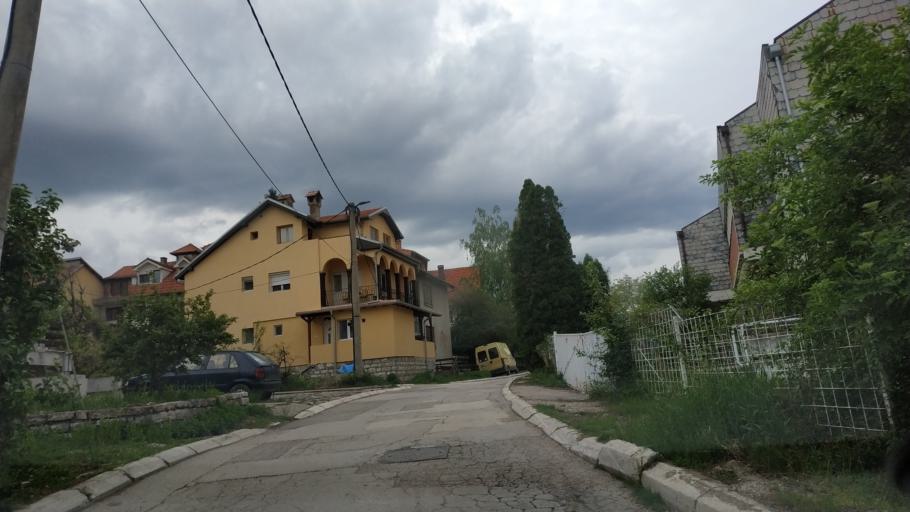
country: RS
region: Central Serbia
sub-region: Zajecarski Okrug
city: Soko Banja
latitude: 43.6427
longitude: 21.8690
